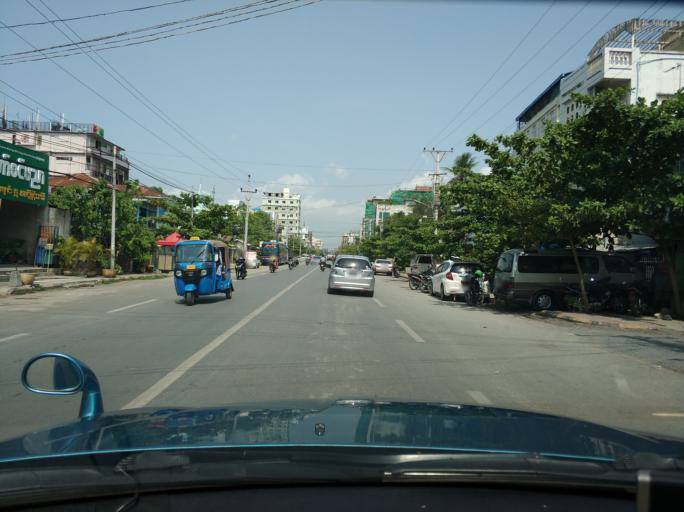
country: MM
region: Mandalay
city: Mandalay
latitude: 21.9657
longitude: 96.0937
